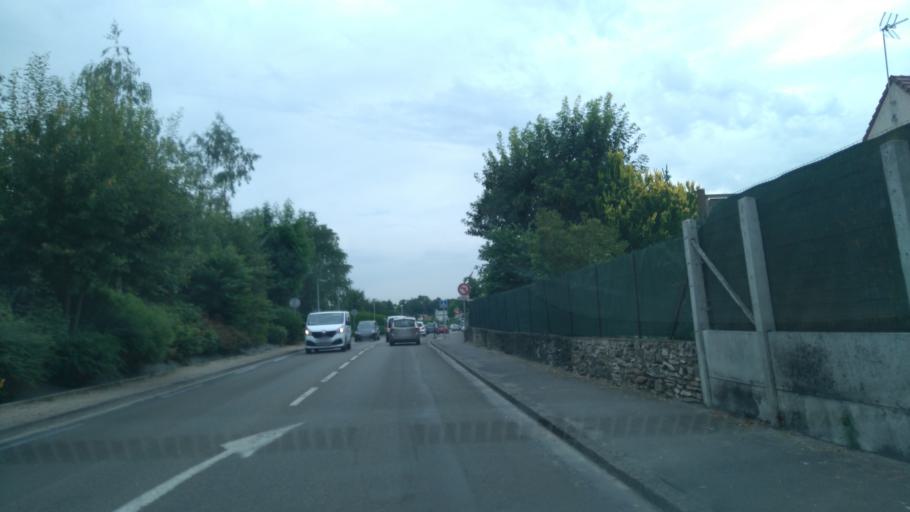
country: FR
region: Picardie
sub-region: Departement de l'Oise
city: Saint-Maximin
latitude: 49.2222
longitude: 2.4551
